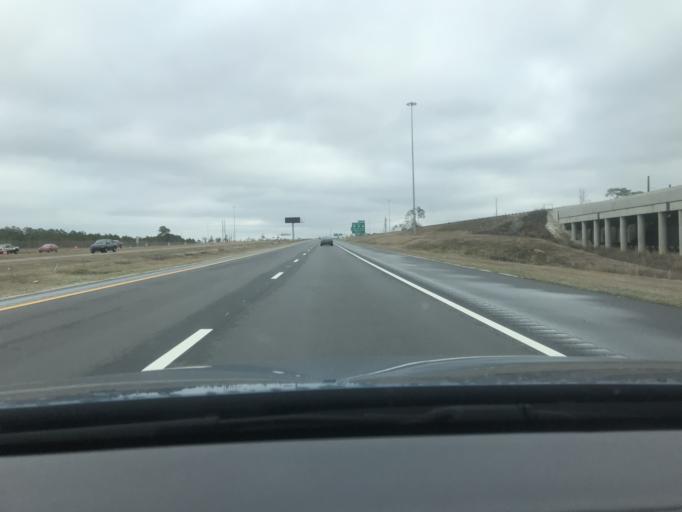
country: US
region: North Carolina
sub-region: Cumberland County
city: Fort Bragg
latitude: 35.1121
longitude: -78.9700
